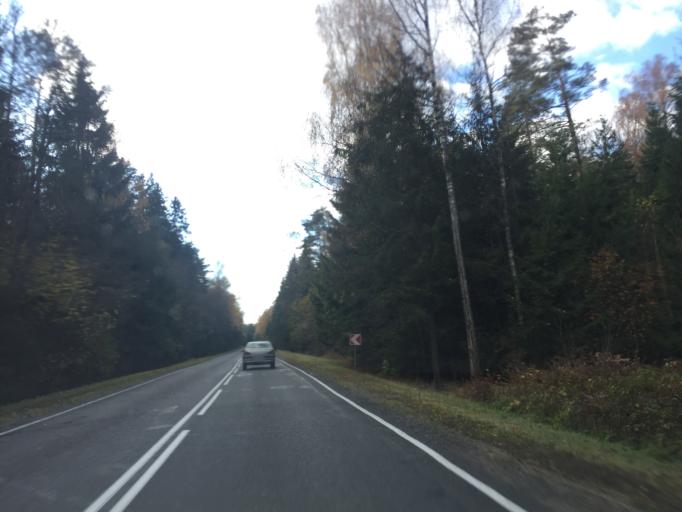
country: BY
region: Minsk
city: Narach
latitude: 54.9279
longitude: 26.5447
